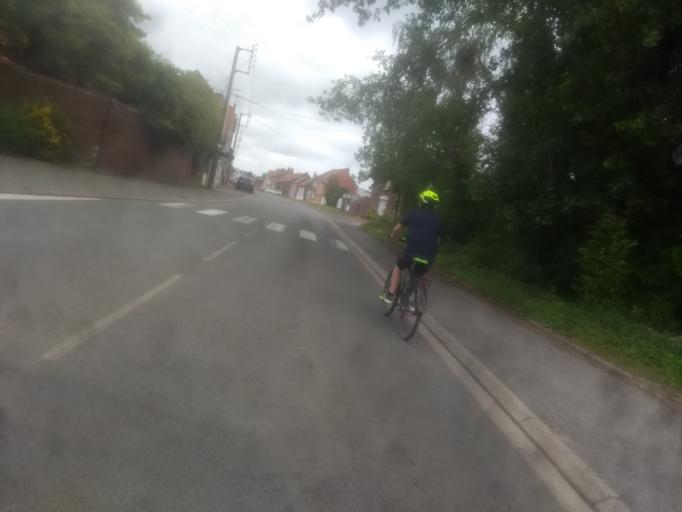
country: FR
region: Nord-Pas-de-Calais
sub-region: Departement du Pas-de-Calais
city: Neuville-Saint-Vaast
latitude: 50.3547
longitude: 2.7543
